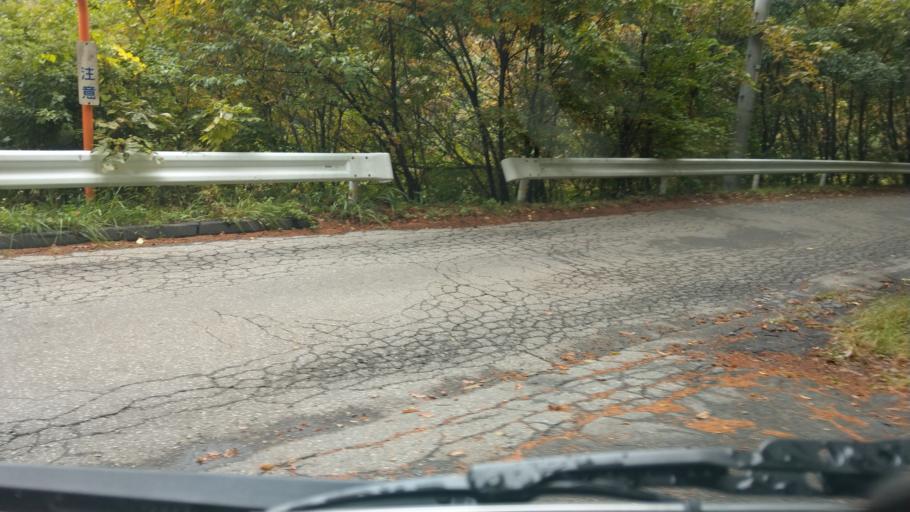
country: JP
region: Nagano
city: Komoro
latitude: 36.3581
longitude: 138.4434
